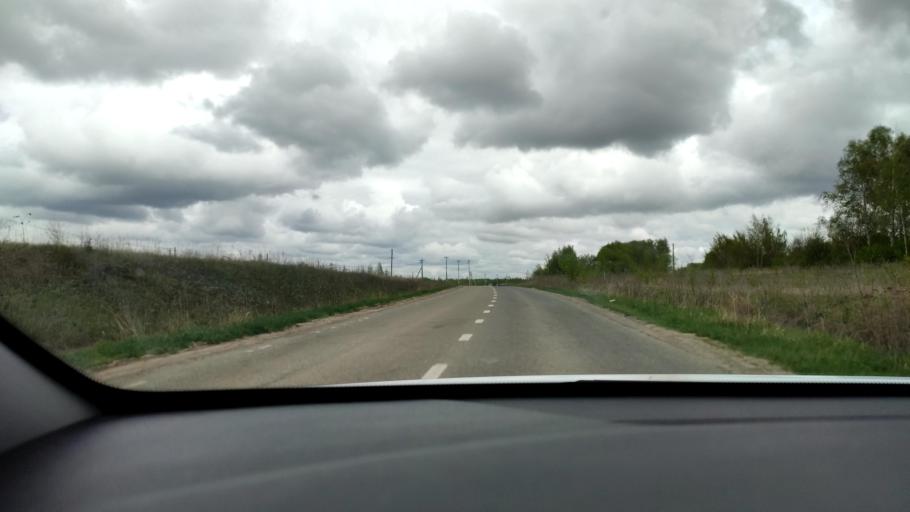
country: RU
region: Tatarstan
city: Vysokaya Gora
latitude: 55.8014
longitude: 49.3084
